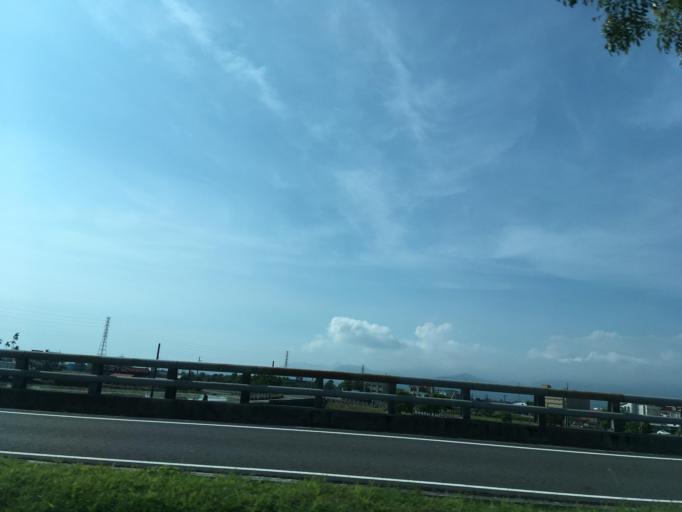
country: TW
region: Taiwan
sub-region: Yilan
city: Yilan
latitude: 24.6782
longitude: 121.7845
